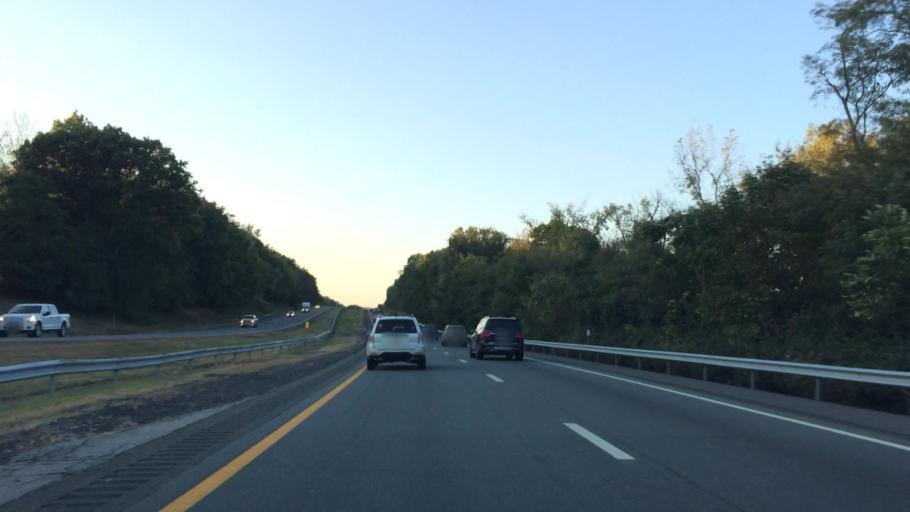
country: US
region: New York
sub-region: Orange County
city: Vails Gate
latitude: 41.4577
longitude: -74.0653
